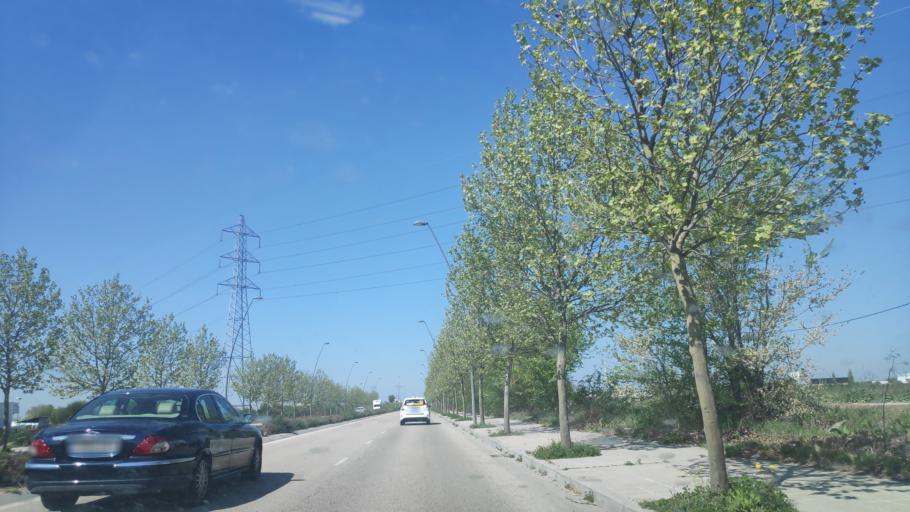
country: ES
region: Madrid
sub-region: Provincia de Madrid
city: Getafe
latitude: 40.2908
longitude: -3.6859
